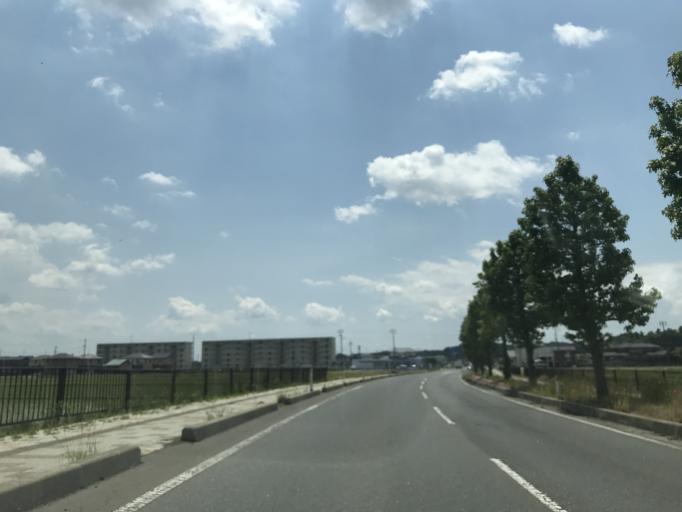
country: JP
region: Miyagi
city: Kogota
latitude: 38.5138
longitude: 141.0647
